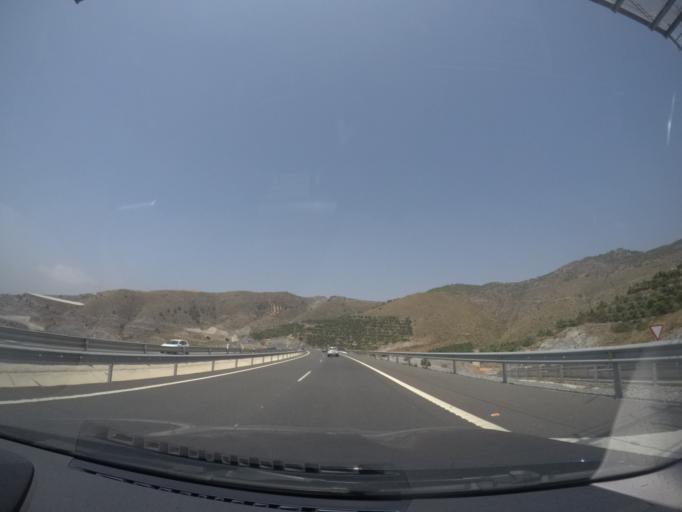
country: ES
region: Andalusia
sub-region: Provincia de Granada
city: Gualchos
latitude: 36.7197
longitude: -3.4305
